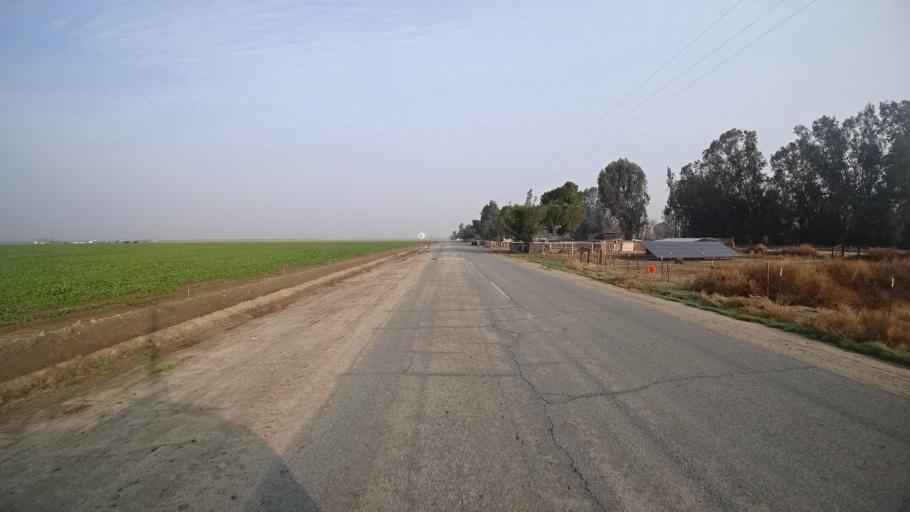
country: US
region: California
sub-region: Kern County
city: Greenfield
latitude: 35.2245
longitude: -119.0215
